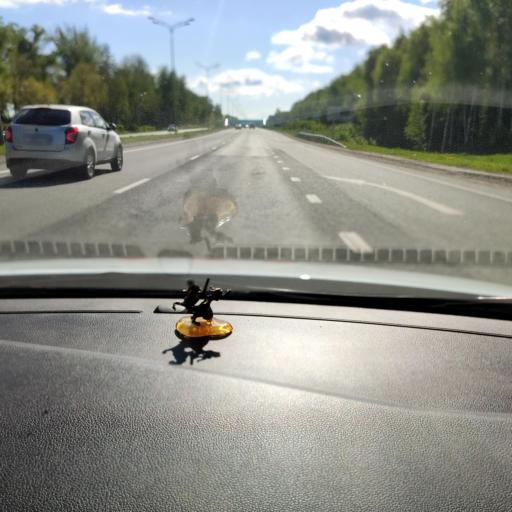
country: RU
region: Tatarstan
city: Osinovo
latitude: 55.8593
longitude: 48.8227
